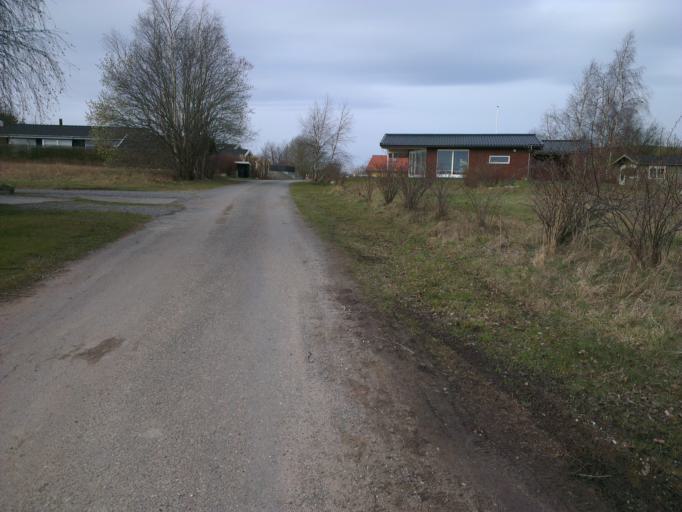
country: DK
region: Capital Region
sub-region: Frederikssund Kommune
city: Frederikssund
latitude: 55.8225
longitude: 12.0335
